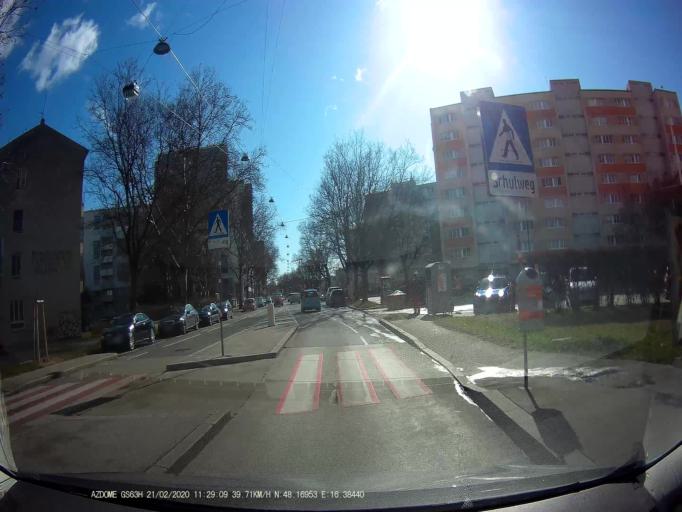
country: AT
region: Vienna
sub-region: Wien Stadt
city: Vienna
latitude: 48.1694
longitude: 16.3845
